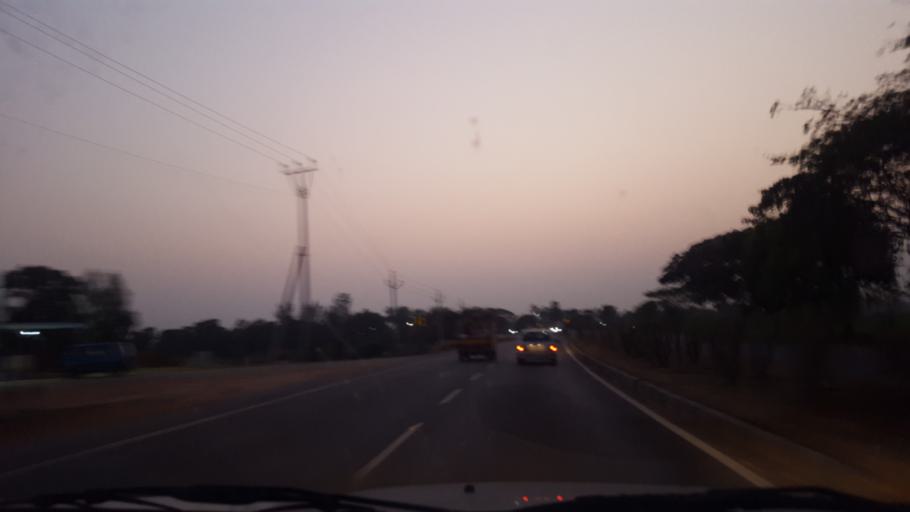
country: IN
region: Andhra Pradesh
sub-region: East Godavari
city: Peddapuram
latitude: 17.1482
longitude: 81.9837
